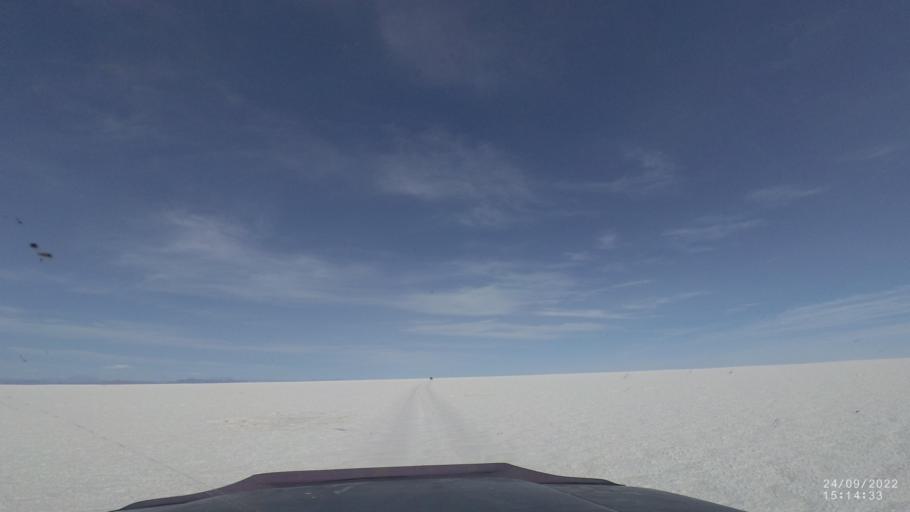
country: BO
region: Potosi
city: Colchani
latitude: -19.9650
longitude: -67.4542
